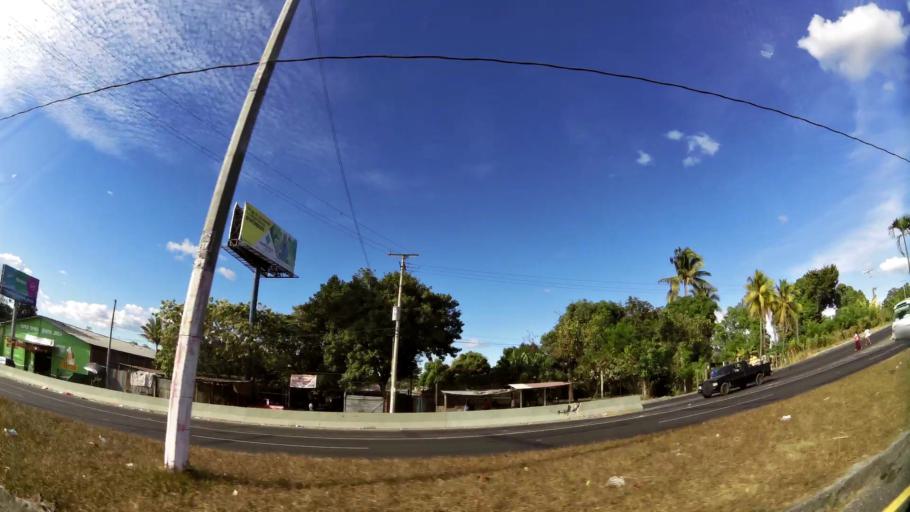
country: SV
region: San Salvador
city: Ilopango
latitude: 13.7358
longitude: -89.0510
